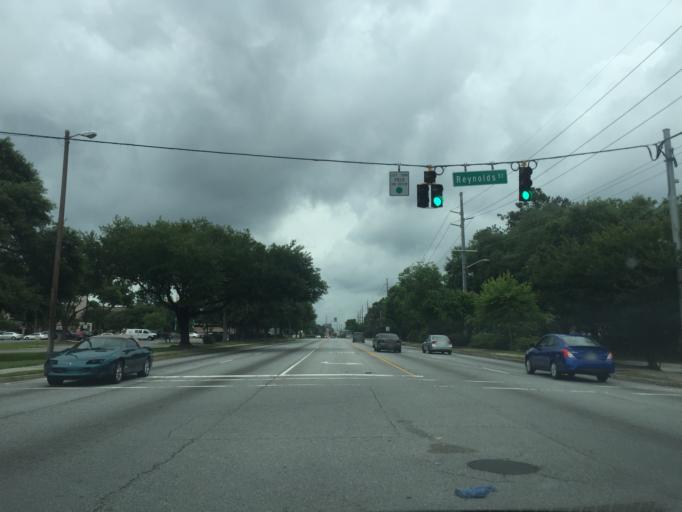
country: US
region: Georgia
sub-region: Chatham County
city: Thunderbolt
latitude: 32.0266
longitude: -81.1021
